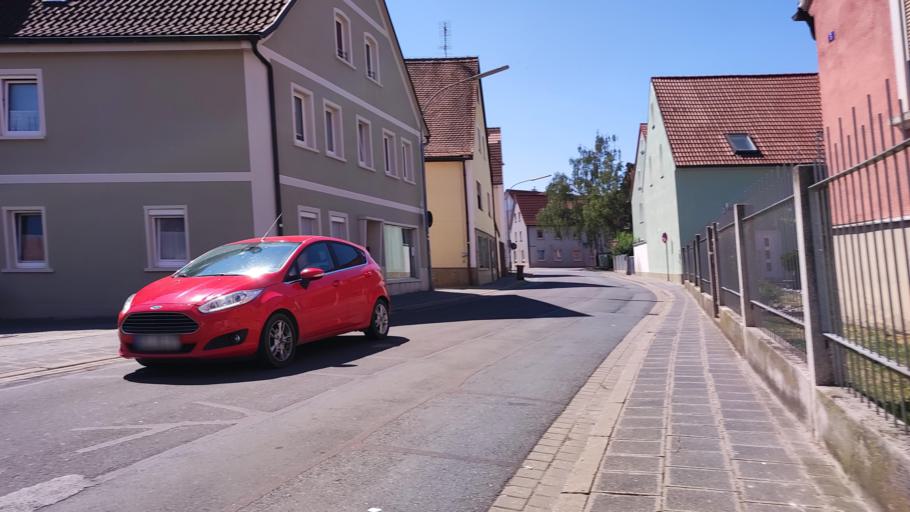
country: DE
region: Bavaria
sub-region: Regierungsbezirk Mittelfranken
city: Neustadt an der Aisch
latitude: 49.5780
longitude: 10.6015
